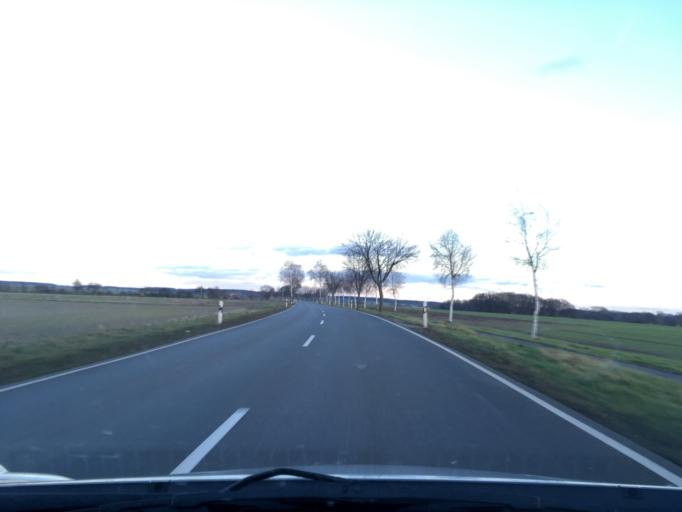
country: DE
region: Lower Saxony
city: Ratzlingen
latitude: 52.9741
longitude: 10.6396
